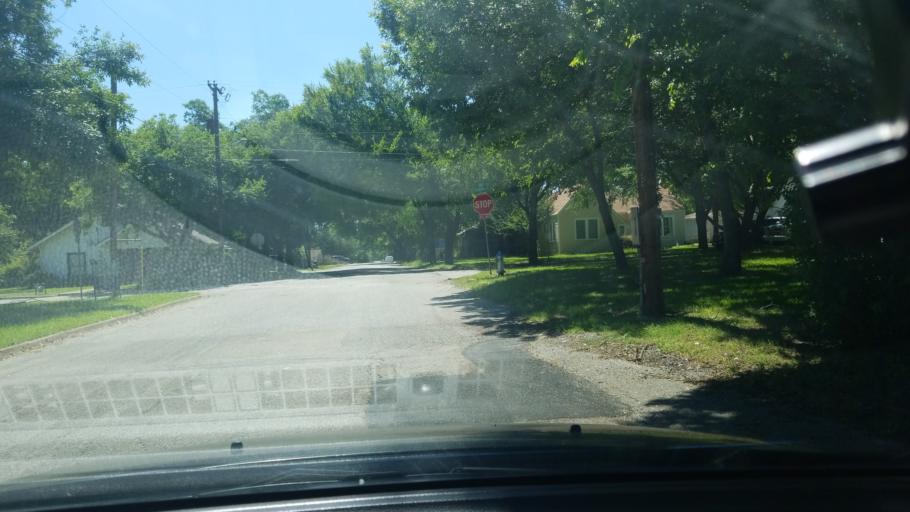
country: US
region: Texas
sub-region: Dallas County
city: Mesquite
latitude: 32.7641
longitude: -96.6021
